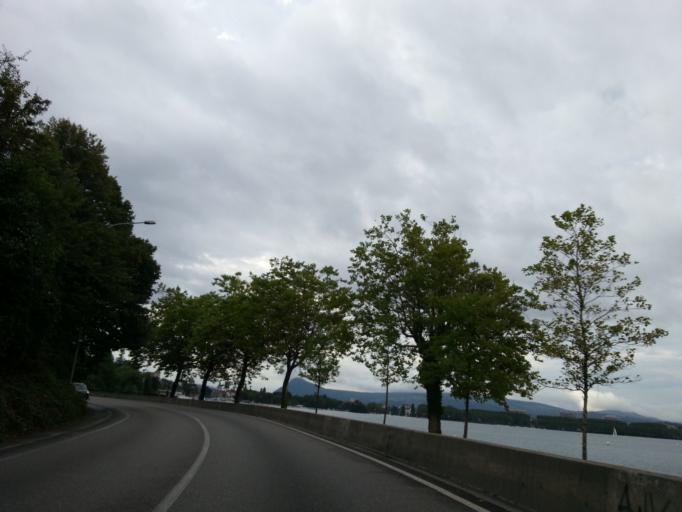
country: FR
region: Rhone-Alpes
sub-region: Departement de la Haute-Savoie
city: Sevrier
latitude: 45.8902
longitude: 6.1433
